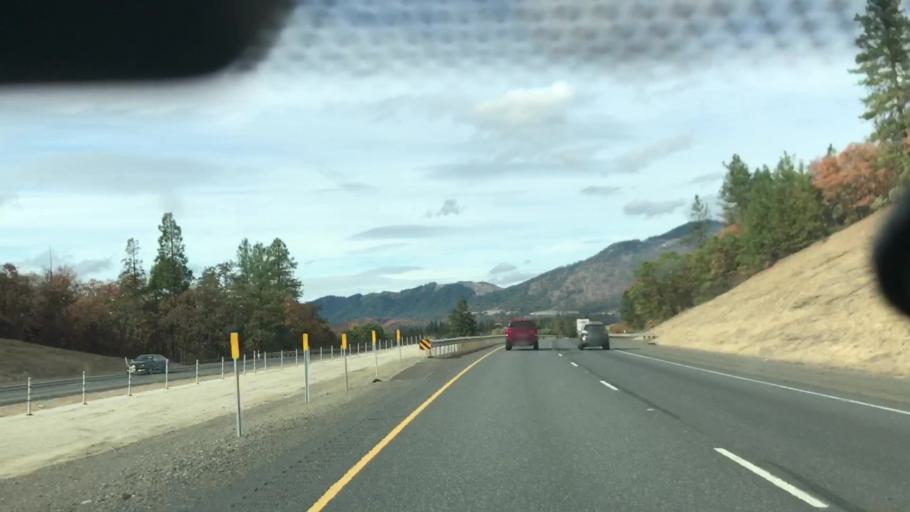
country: US
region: Oregon
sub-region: Josephine County
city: Merlin
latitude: 42.5295
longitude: -123.3690
